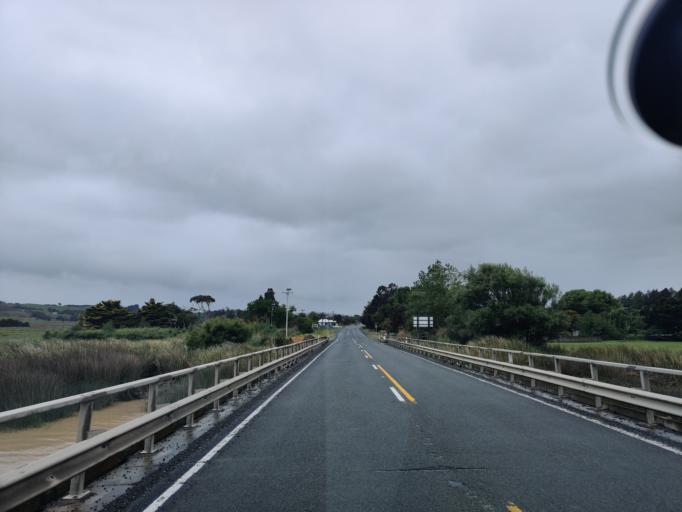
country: NZ
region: Northland
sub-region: Kaipara District
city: Dargaville
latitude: -35.9408
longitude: 173.8852
